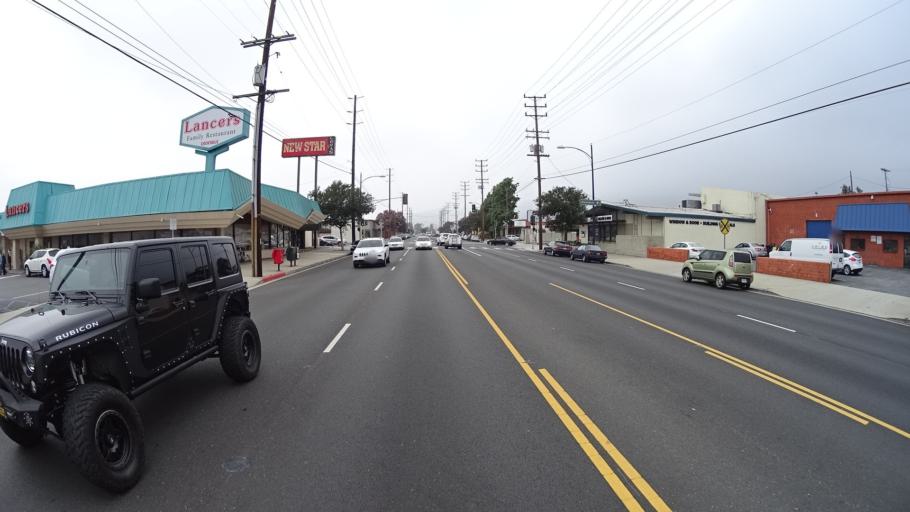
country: US
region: California
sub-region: Los Angeles County
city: Burbank
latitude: 34.1802
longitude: -118.3196
